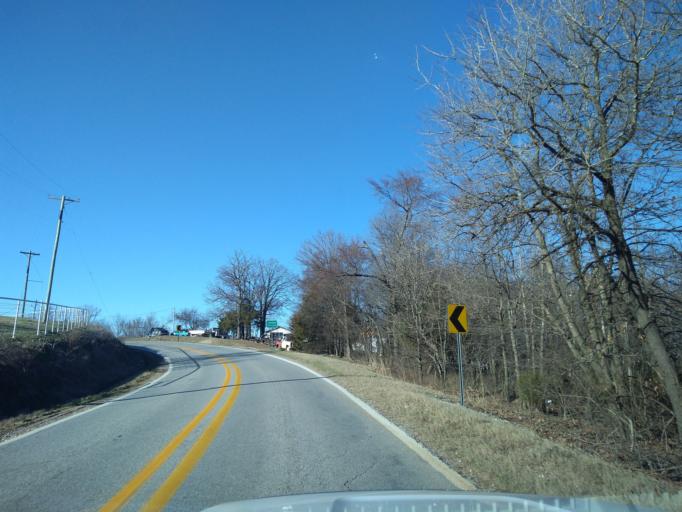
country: US
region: Arkansas
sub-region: Washington County
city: Lincoln
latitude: 35.9496
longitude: -94.3769
